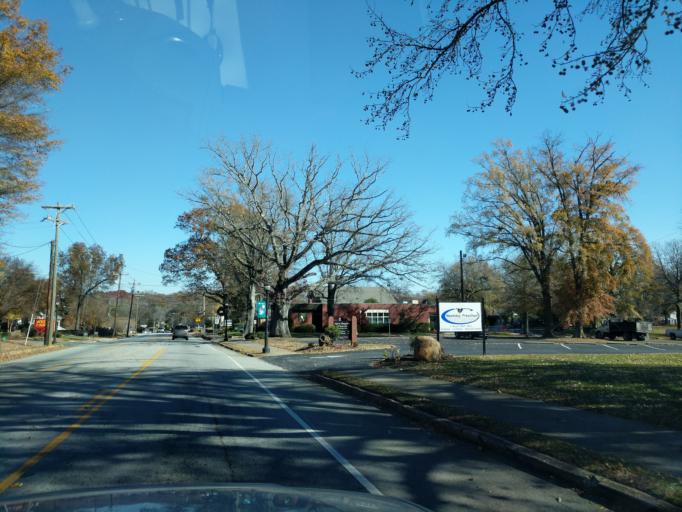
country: US
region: South Carolina
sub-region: Spartanburg County
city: Landrum
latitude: 35.1756
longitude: -82.1867
